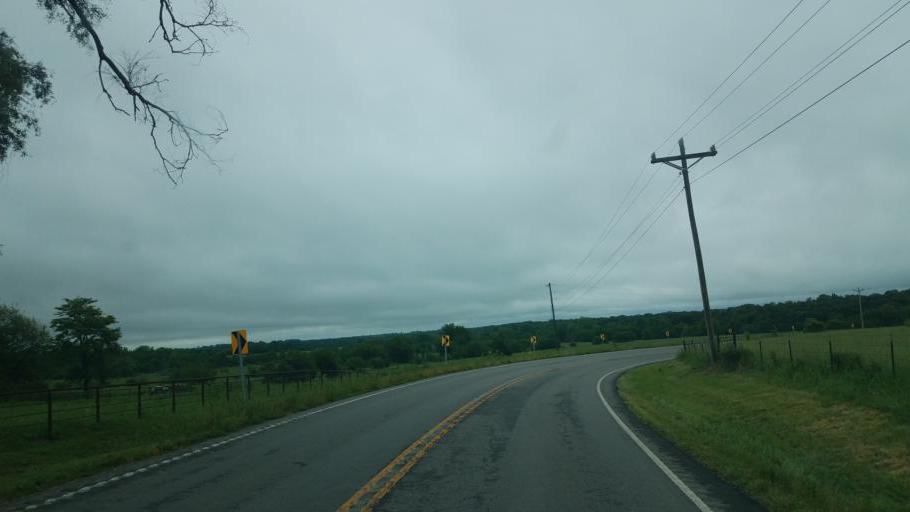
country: US
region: Missouri
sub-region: Miller County
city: Eldon
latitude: 38.4696
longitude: -92.5636
